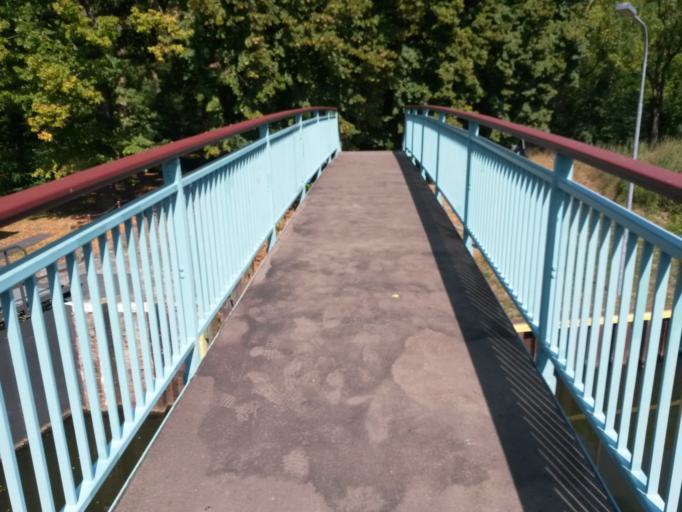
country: DE
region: Saxony-Anhalt
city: Jerichow
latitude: 52.4031
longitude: 11.9789
